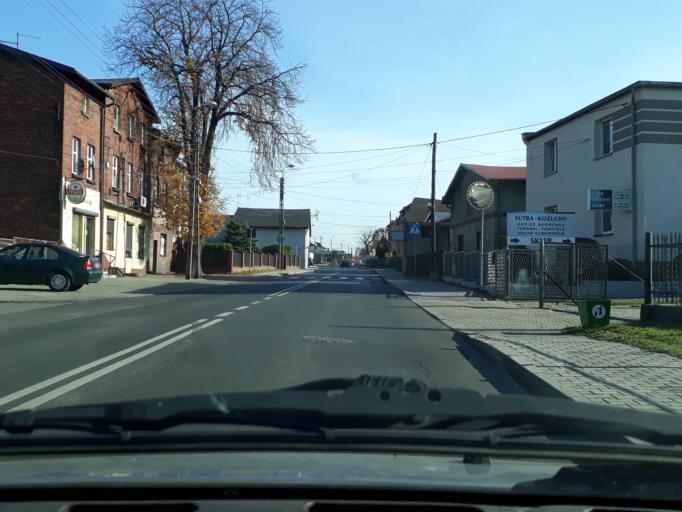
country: PL
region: Silesian Voivodeship
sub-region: Powiat tarnogorski
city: Tarnowskie Gory
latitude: 50.4219
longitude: 18.8744
